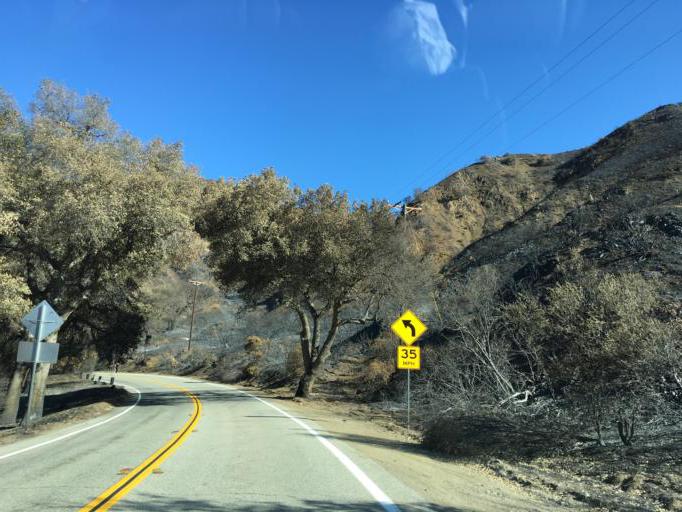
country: US
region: California
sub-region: Los Angeles County
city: San Fernando
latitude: 34.3800
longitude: -118.4026
